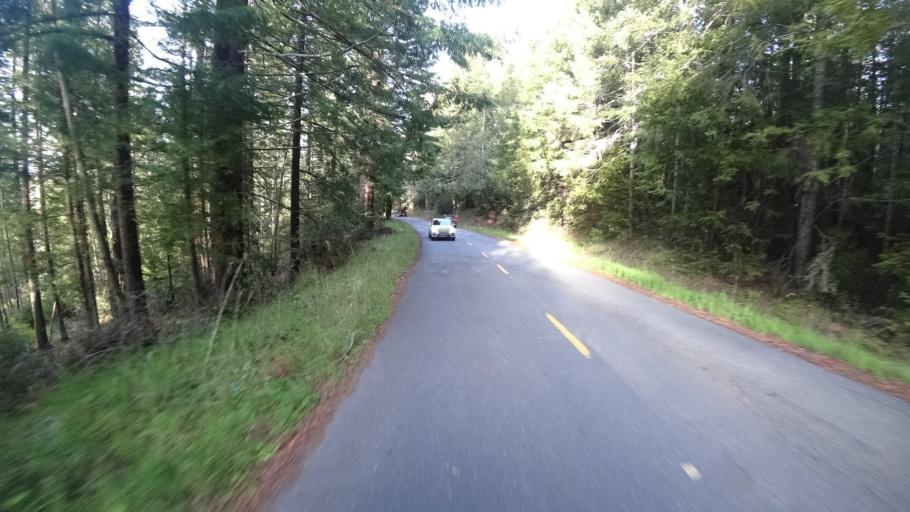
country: US
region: California
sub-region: Humboldt County
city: Bayside
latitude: 40.7596
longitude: -124.0169
